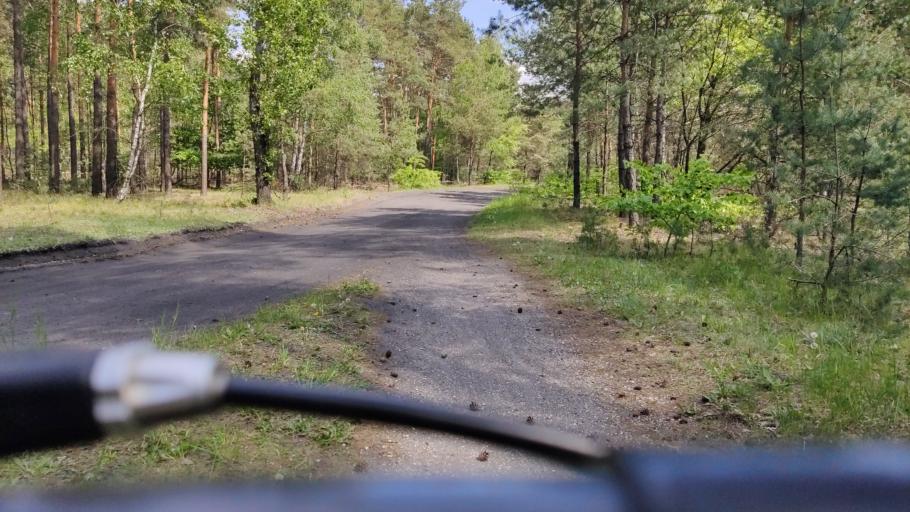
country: PL
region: Kujawsko-Pomorskie
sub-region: Wloclawek
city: Wloclawek
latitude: 52.6356
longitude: 19.1213
